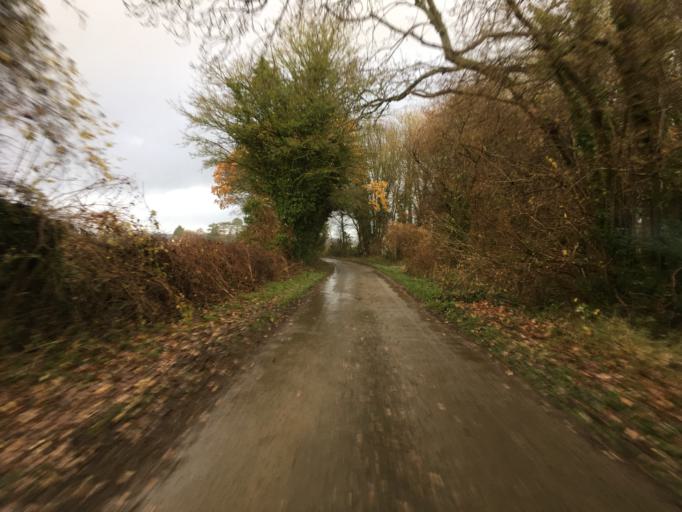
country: GB
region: England
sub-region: Wiltshire
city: Hankerton
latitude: 51.6521
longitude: -2.0679
